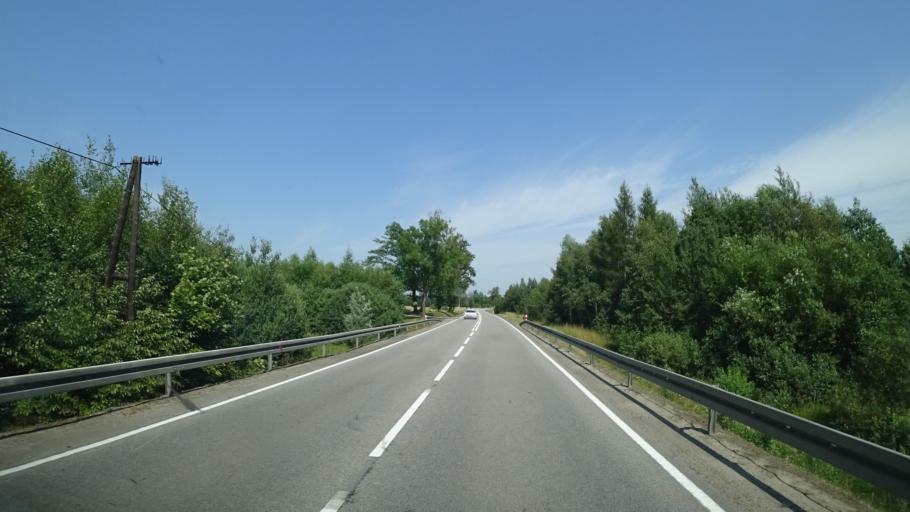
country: PL
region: Pomeranian Voivodeship
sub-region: Powiat koscierski
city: Koscierzyna
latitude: 54.1521
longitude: 18.0302
